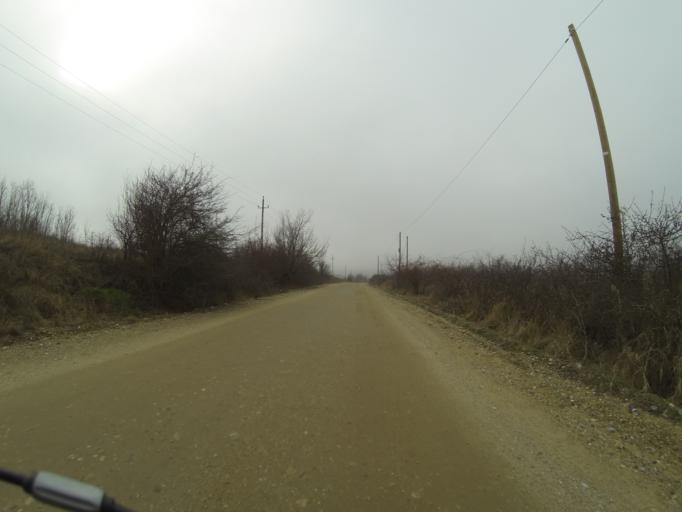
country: RO
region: Mehedinti
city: Dumbrava de Sus
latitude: 44.4889
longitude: 23.0803
